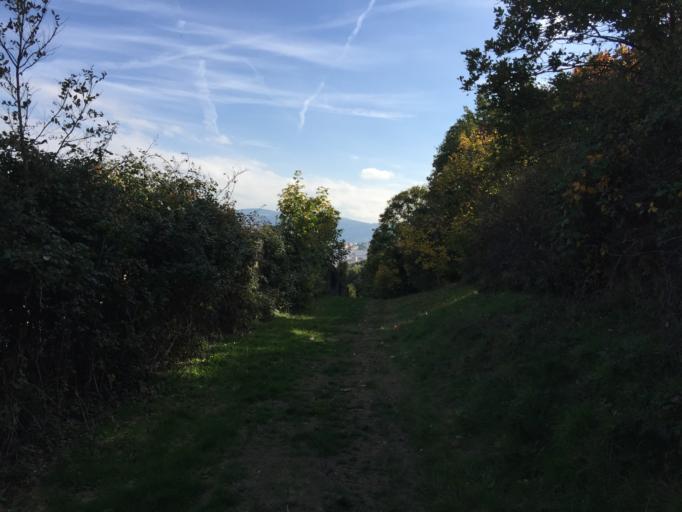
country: FR
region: Rhone-Alpes
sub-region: Departement de la Loire
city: Saint-Priest-en-Jarez
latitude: 45.4527
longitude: 4.3757
